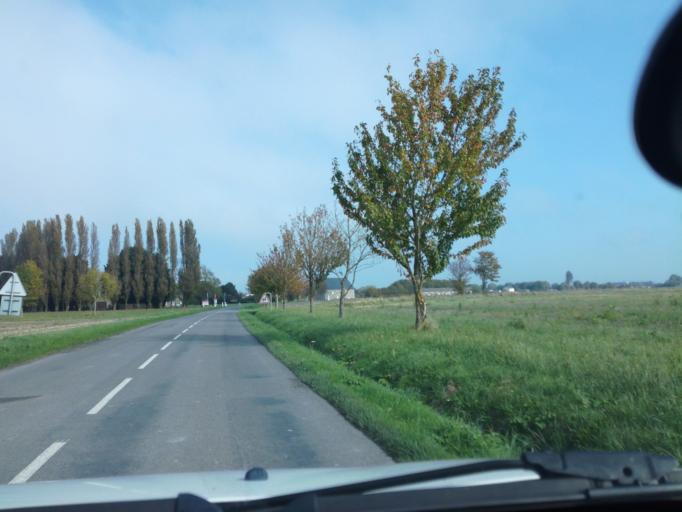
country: FR
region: Brittany
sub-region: Departement d'Ille-et-Vilaine
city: Cherrueix
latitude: 48.5994
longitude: -1.7135
